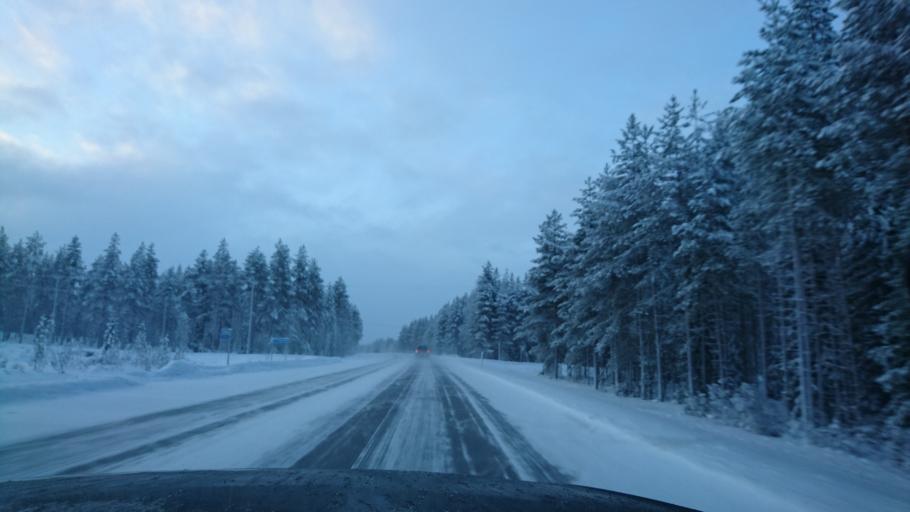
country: FI
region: Kainuu
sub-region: Kehys-Kainuu
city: Puolanka
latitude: 65.4642
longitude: 27.6479
